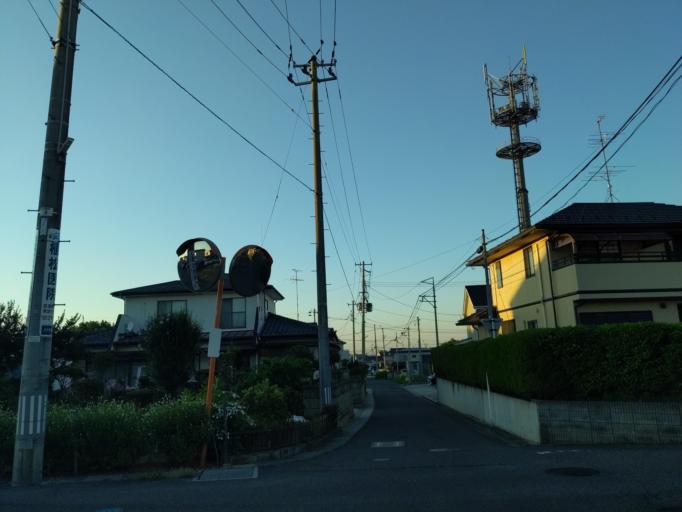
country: JP
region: Fukushima
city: Koriyama
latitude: 37.4117
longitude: 140.3311
